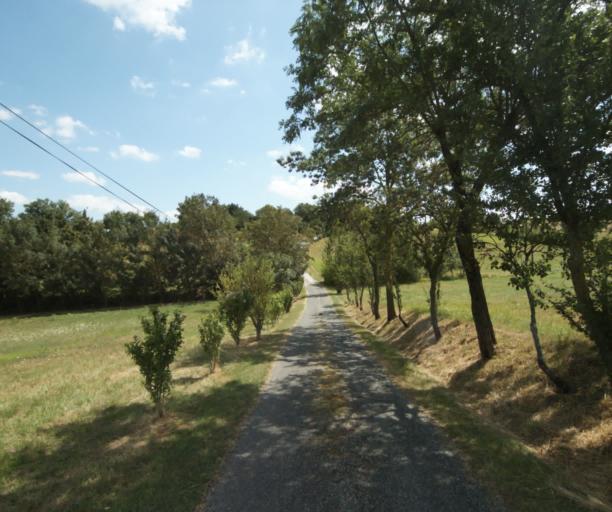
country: FR
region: Midi-Pyrenees
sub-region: Departement de la Haute-Garonne
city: Auriac-sur-Vendinelle
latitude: 43.4768
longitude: 1.7972
